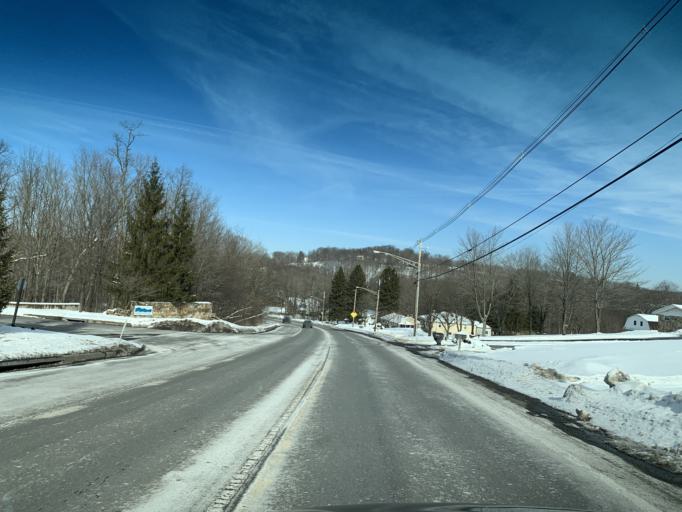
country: US
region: Maryland
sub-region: Allegany County
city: Frostburg
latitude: 39.6419
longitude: -78.9395
